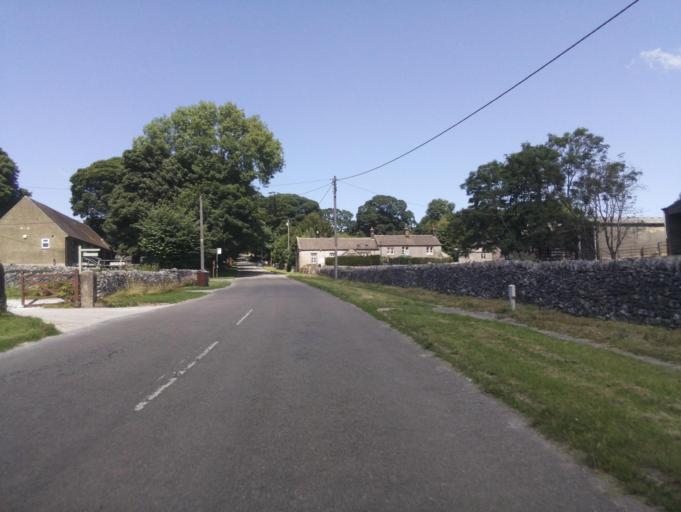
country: GB
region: England
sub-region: Derbyshire
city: Tideswell
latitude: 53.2662
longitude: -1.8175
